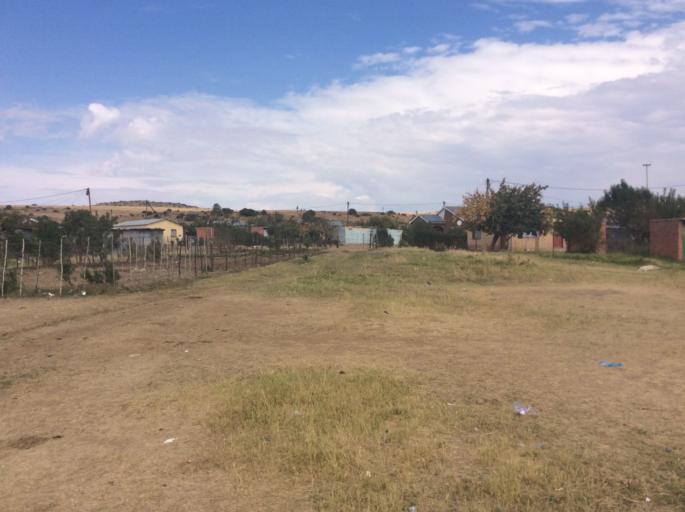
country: ZA
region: Orange Free State
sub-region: Xhariep District Municipality
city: Dewetsdorp
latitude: -29.5795
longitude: 26.6892
